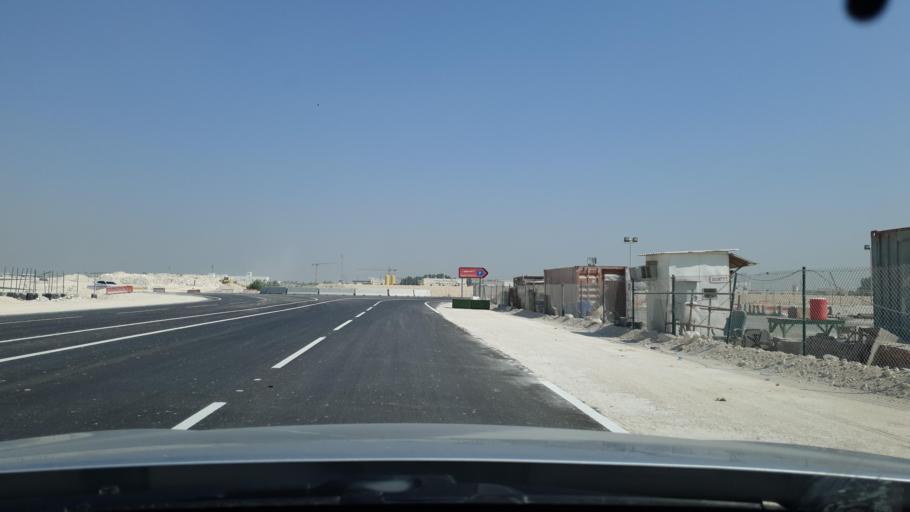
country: QA
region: Baladiyat ad Dawhah
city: Doha
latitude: 25.2242
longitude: 51.5204
